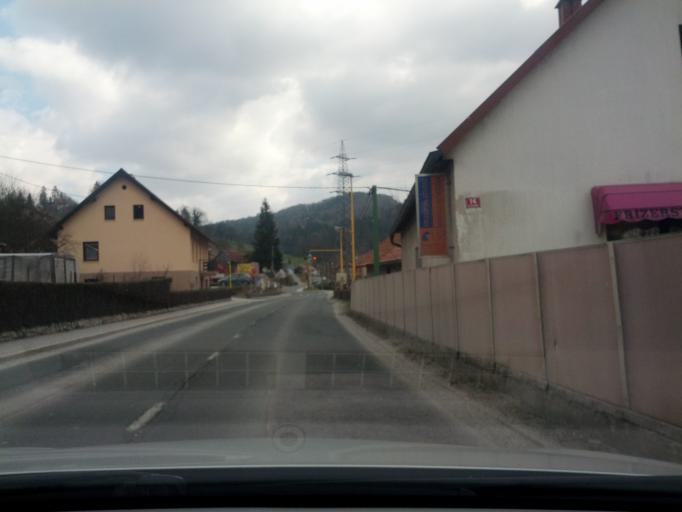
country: SI
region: Hrastnik
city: Dol pri Hrastniku
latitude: 46.1404
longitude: 15.1194
